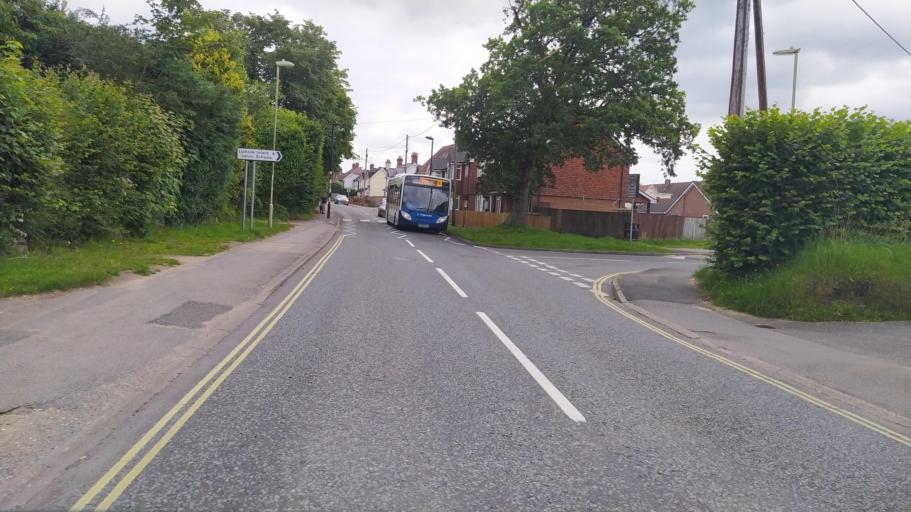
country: GB
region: England
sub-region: Hampshire
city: Liphook
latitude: 51.0820
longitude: -0.8051
